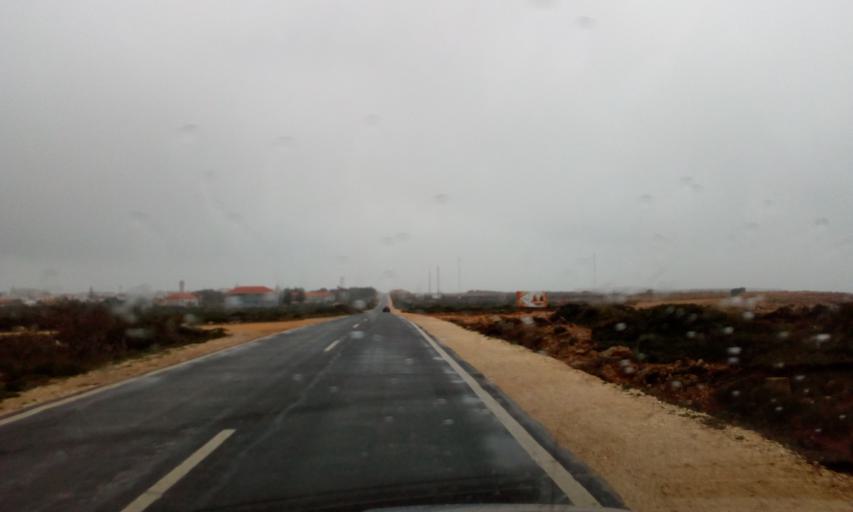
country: PT
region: Faro
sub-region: Vila do Bispo
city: Sagres
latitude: 37.0152
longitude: -8.9534
